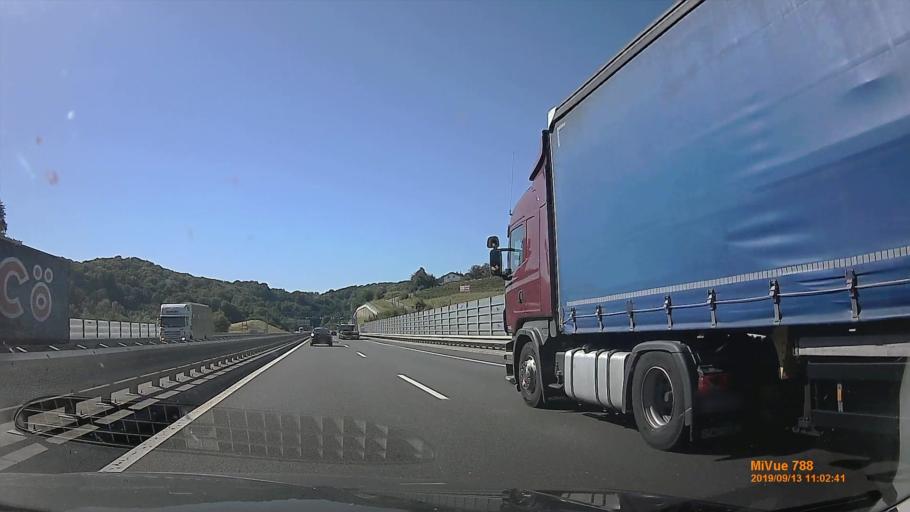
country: SI
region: Pesnica
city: Pesnica pri Mariboru
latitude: 46.5740
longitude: 15.6873
